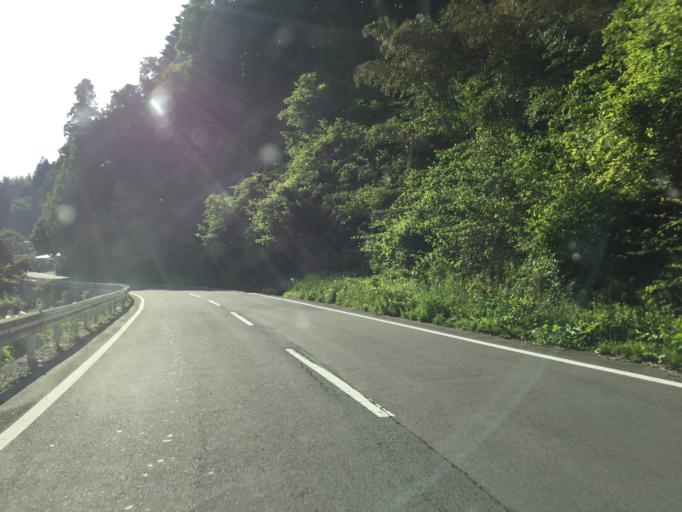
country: JP
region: Ibaraki
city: Daigo
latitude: 36.9253
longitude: 140.4741
